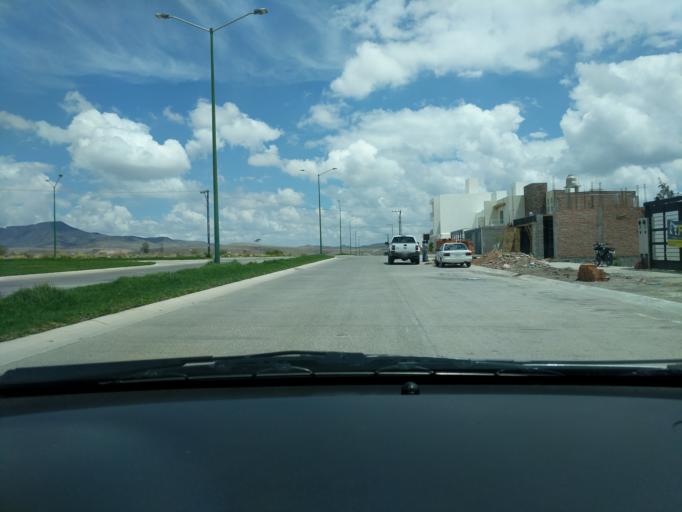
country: MX
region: San Luis Potosi
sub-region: Mexquitic de Carmona
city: Guadalupe Victoria
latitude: 22.1587
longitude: -101.0545
